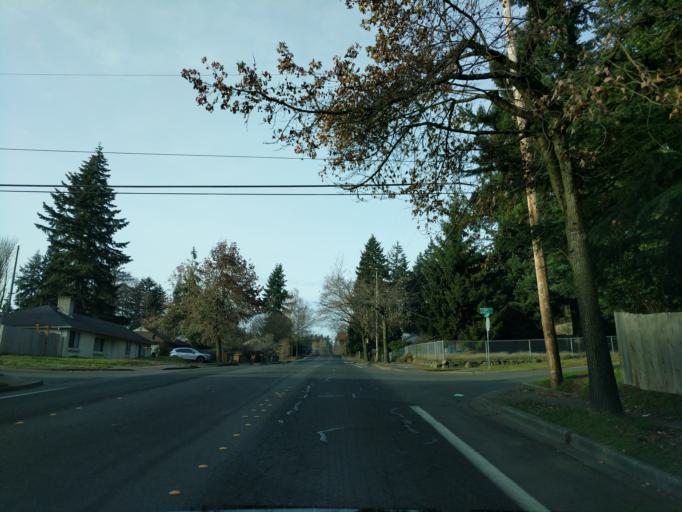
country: US
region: Washington
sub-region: King County
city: Shoreline
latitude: 47.7414
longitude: -122.3396
